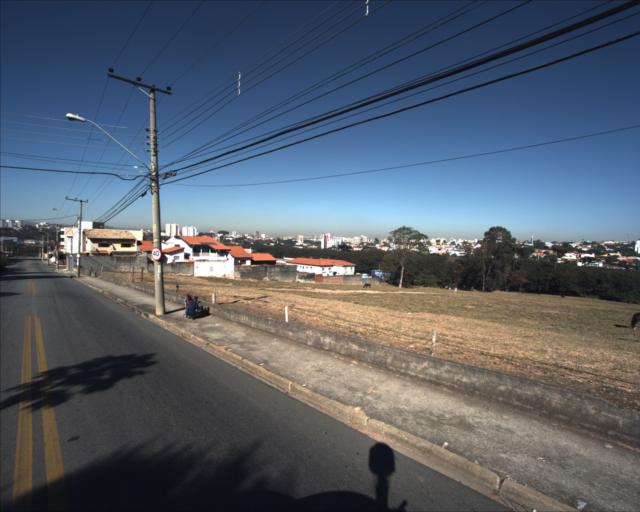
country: BR
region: Sao Paulo
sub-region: Sorocaba
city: Sorocaba
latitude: -23.4816
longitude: -47.4361
